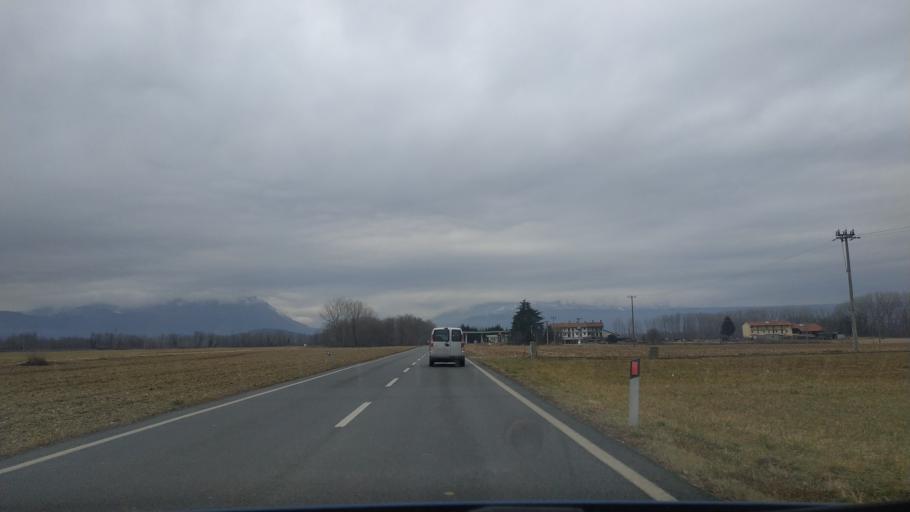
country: IT
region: Piedmont
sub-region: Provincia di Torino
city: Romano Canavese
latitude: 45.4052
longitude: 7.8828
